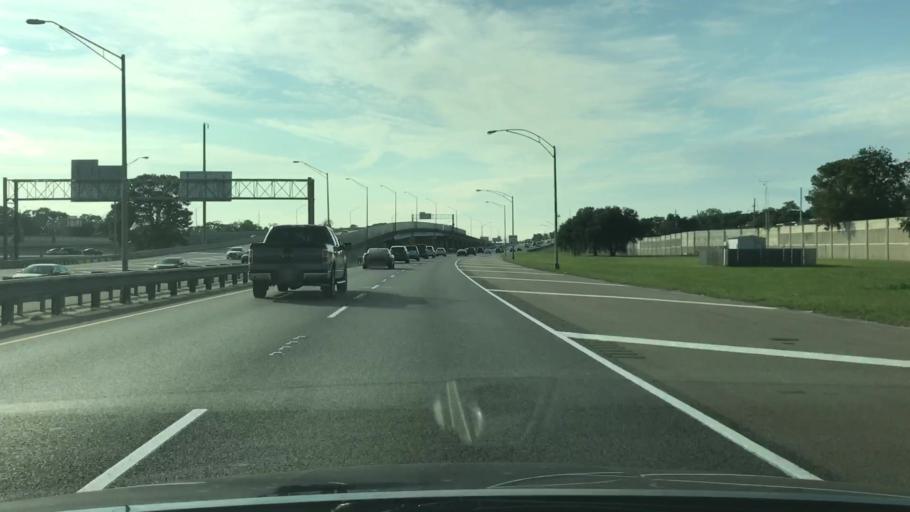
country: US
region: Louisiana
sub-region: Jefferson Parish
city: Metairie
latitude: 29.9957
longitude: -90.1173
